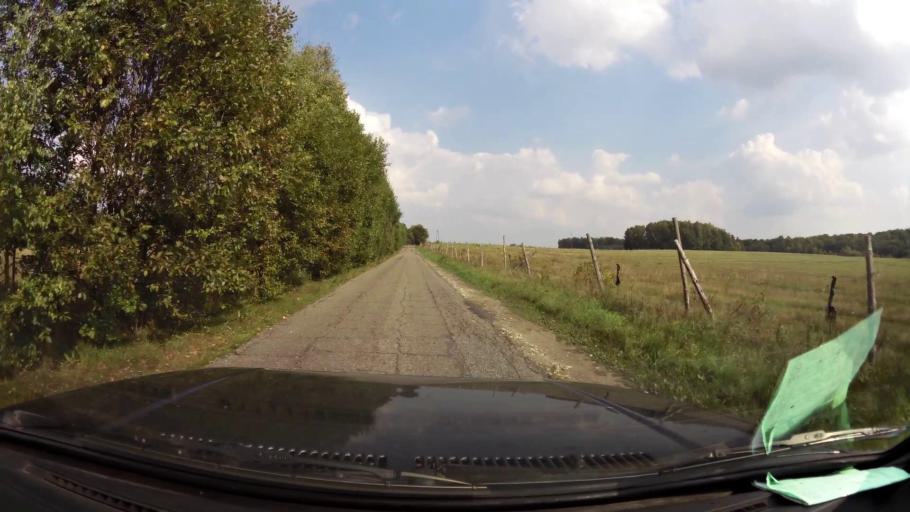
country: PL
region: West Pomeranian Voivodeship
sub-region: Powiat koszalinski
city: Polanow
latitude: 54.1172
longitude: 16.5099
